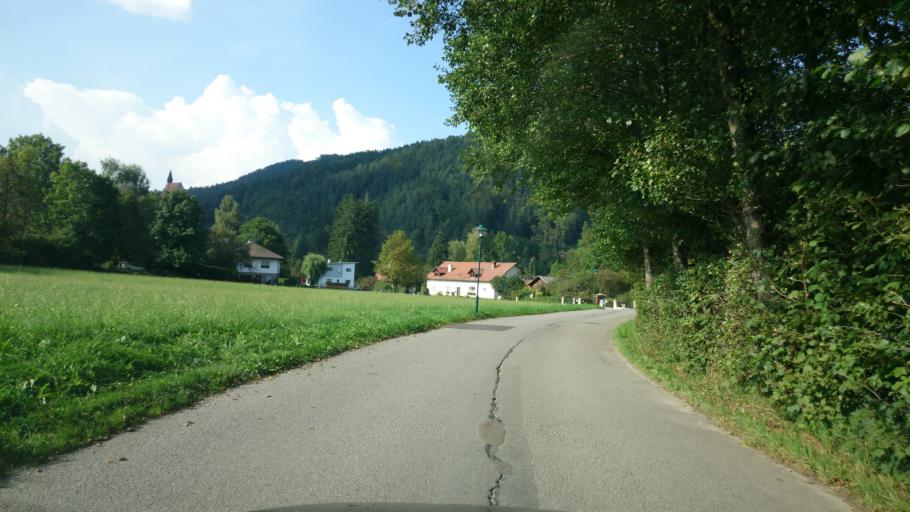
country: AT
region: Lower Austria
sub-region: Politischer Bezirk Neunkirchen
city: Kirchberg am Wechsel
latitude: 47.6046
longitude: 16.0051
